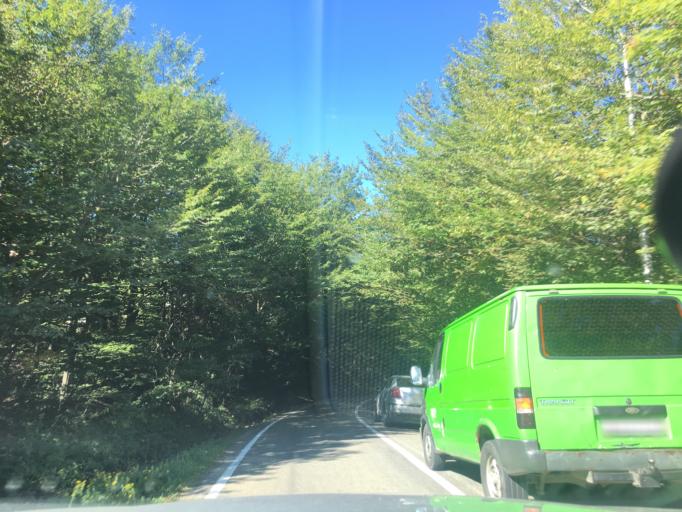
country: GE
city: Didi Lilo
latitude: 41.8760
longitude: 44.9119
